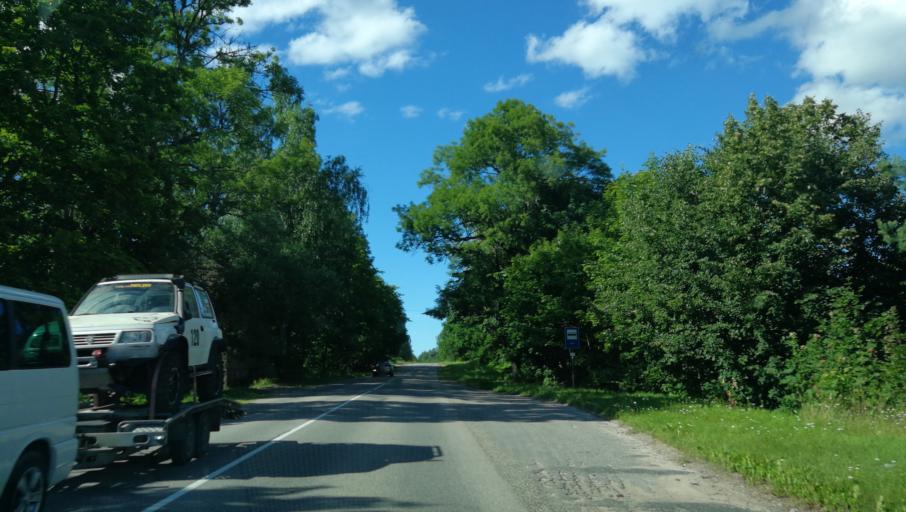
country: LV
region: Madonas Rajons
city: Madona
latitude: 56.8686
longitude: 26.1809
